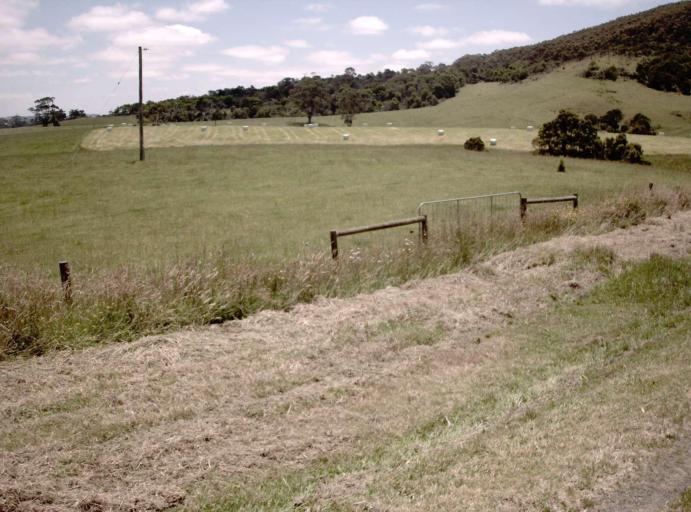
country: AU
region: Victoria
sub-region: Bass Coast
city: North Wonthaggi
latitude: -38.7172
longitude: 146.1095
